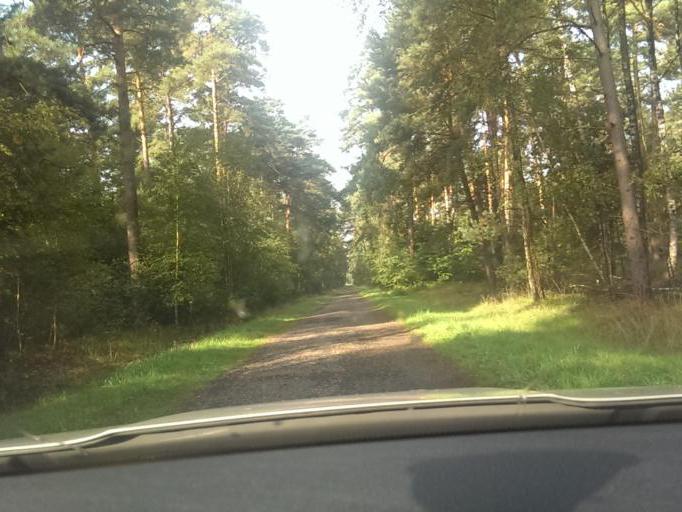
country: DE
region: Lower Saxony
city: Elze
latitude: 52.5808
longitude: 9.7889
